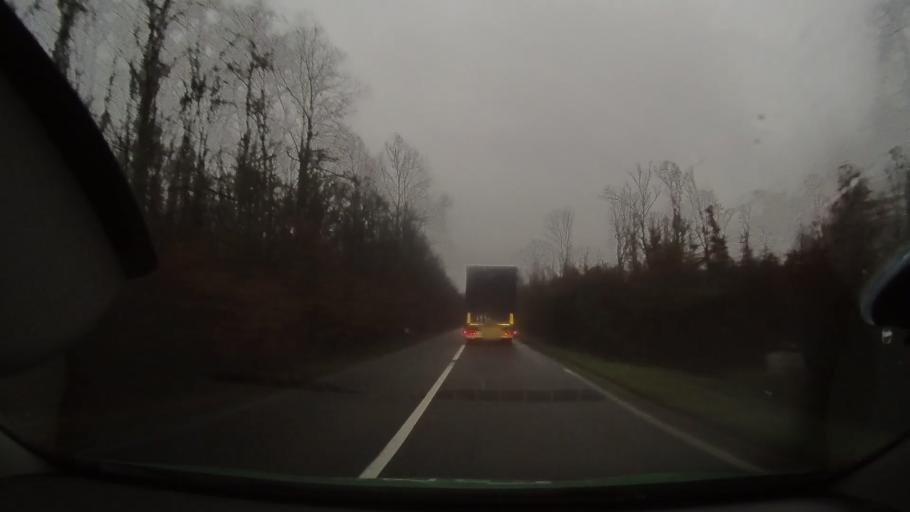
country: RO
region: Arad
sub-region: Comuna Beliu
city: Beliu
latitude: 46.5092
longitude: 21.9670
